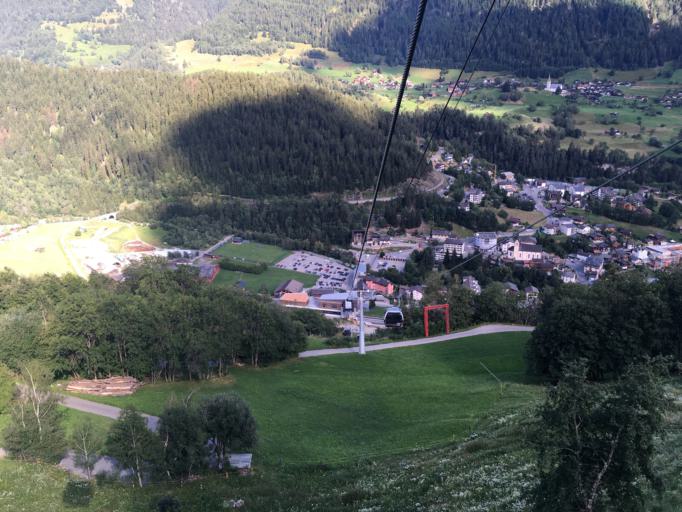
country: CH
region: Valais
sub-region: Goms District
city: Fiesch
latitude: 46.4075
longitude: 8.1278
